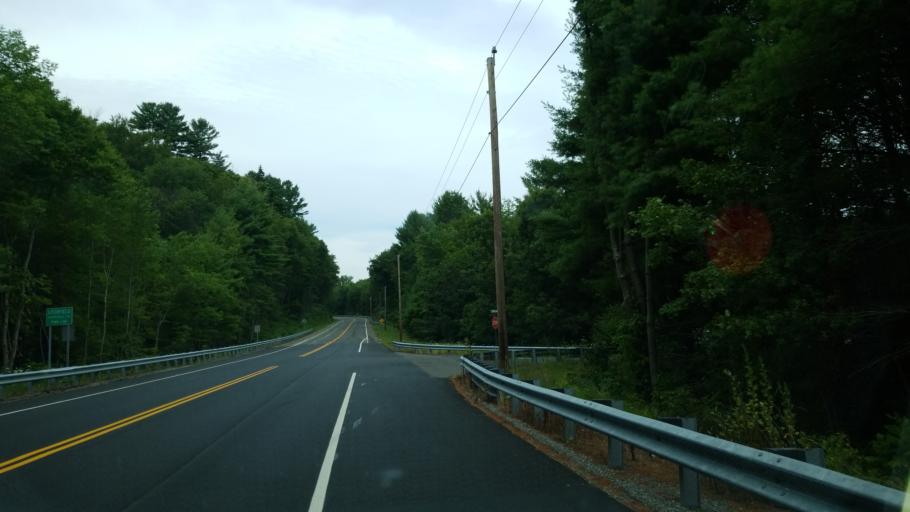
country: US
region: Connecticut
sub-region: Litchfield County
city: Thomaston
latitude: 41.6925
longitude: -73.0990
